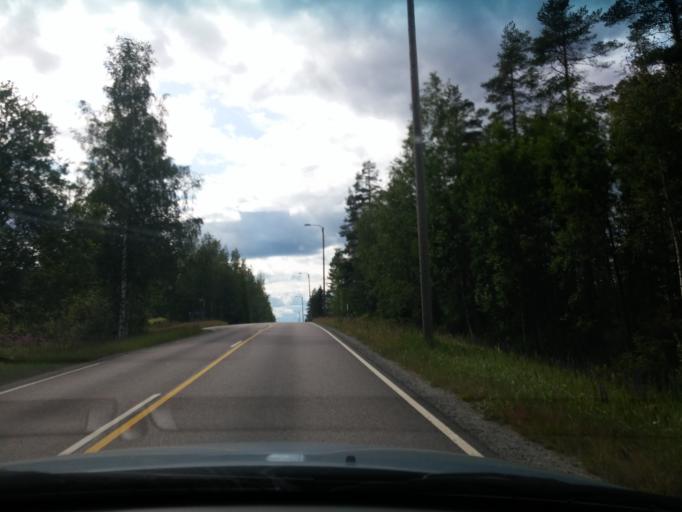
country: FI
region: Central Finland
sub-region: Saarijaervi-Viitasaari
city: Pylkoenmaeki
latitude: 62.6183
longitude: 24.7570
